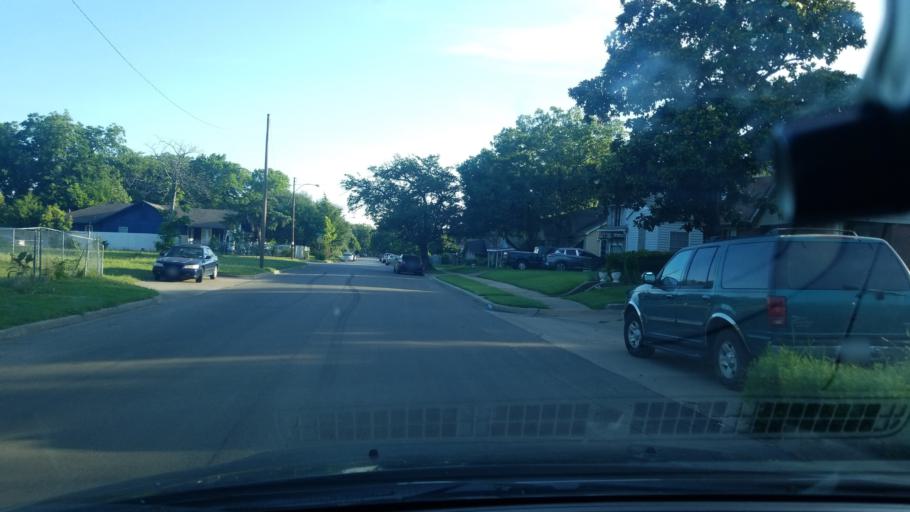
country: US
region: Texas
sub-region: Dallas County
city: Dallas
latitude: 32.7244
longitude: -96.8216
